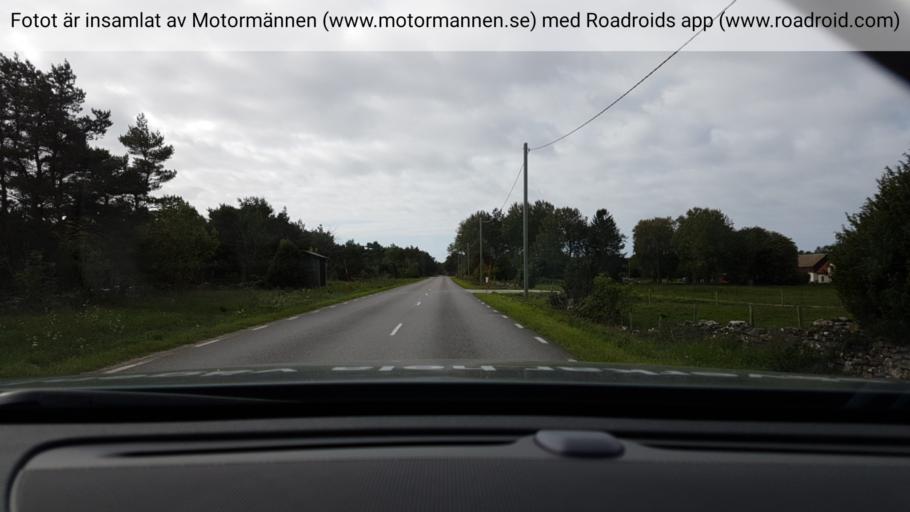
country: SE
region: Gotland
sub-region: Gotland
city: Hemse
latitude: 56.9615
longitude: 18.2222
